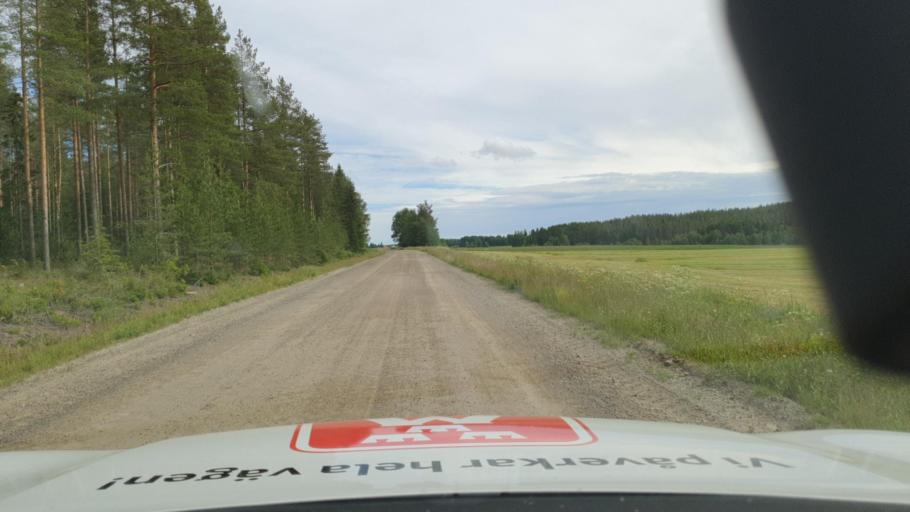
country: SE
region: Vaesterbotten
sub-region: Skelleftea Kommun
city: Burea
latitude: 64.3455
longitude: 21.1194
